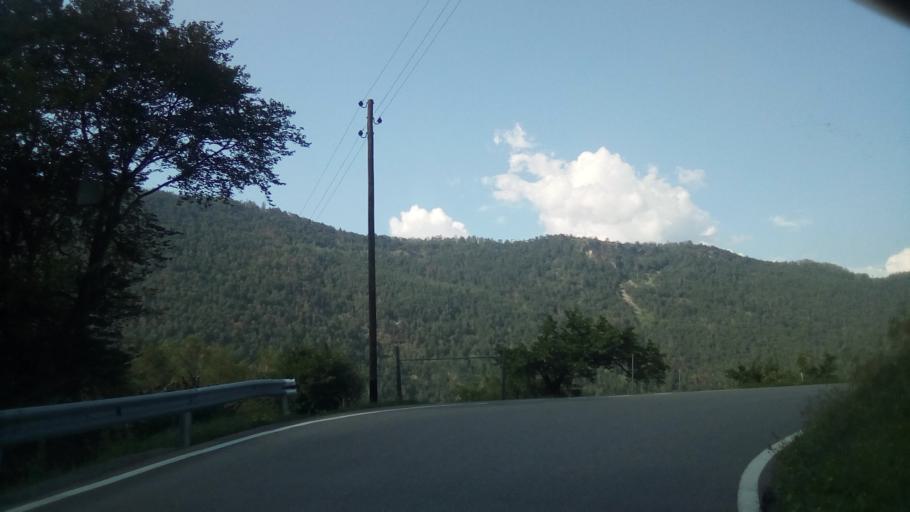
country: CH
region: Valais
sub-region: Martigny District
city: Martigny-Combe
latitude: 46.0724
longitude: 7.0744
